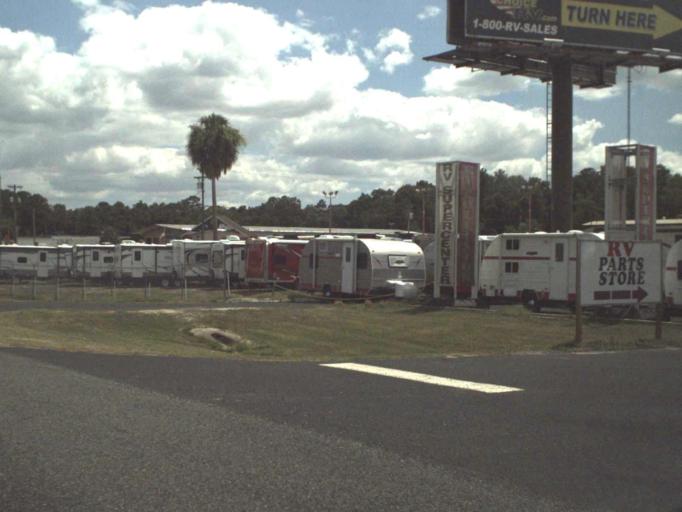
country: US
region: Florida
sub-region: Marion County
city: Ocala
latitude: 29.2191
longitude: -82.1464
